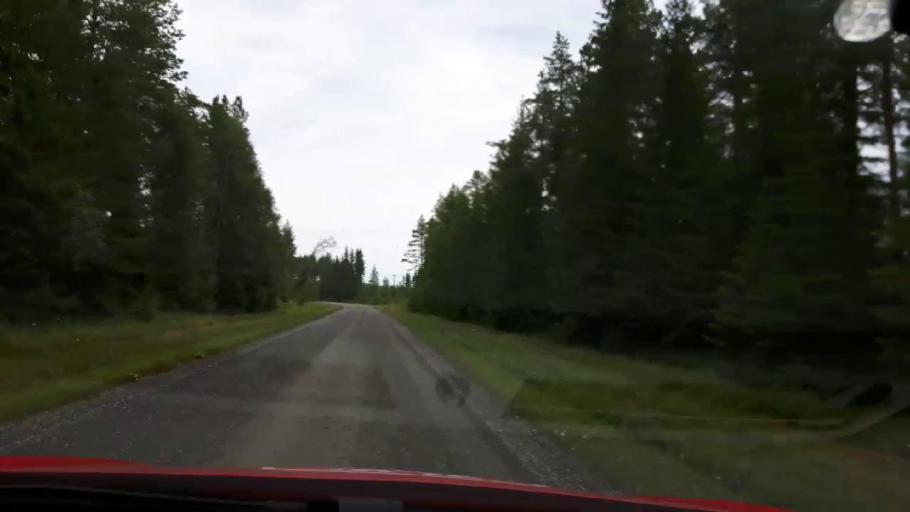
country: SE
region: Jaemtland
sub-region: Stroemsunds Kommun
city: Stroemsund
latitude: 63.7412
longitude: 15.5737
